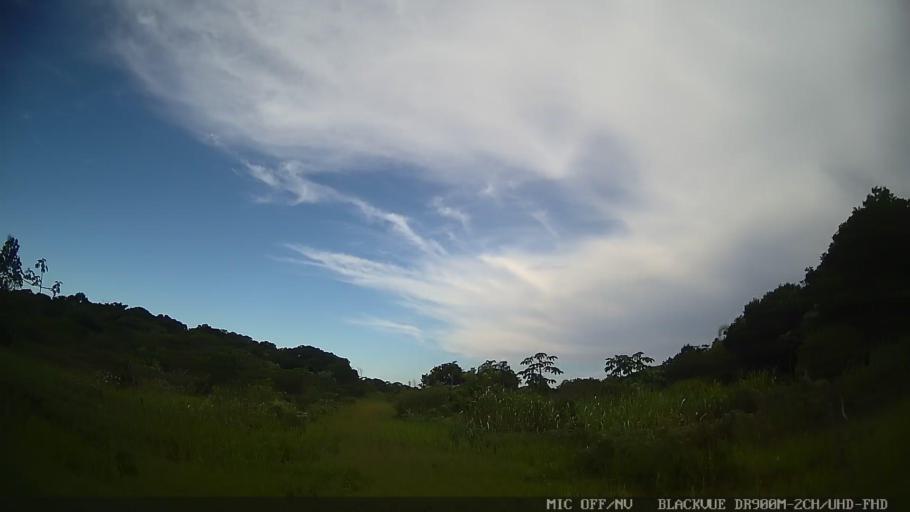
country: BR
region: Sao Paulo
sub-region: Iguape
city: Iguape
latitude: -24.6566
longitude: -47.4095
